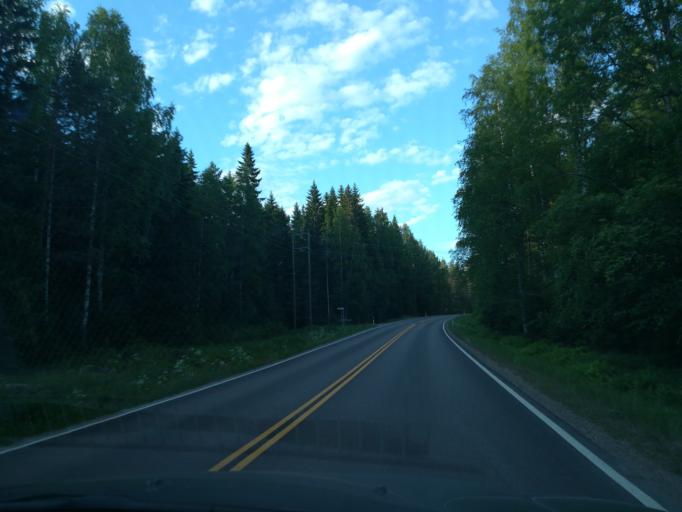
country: FI
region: Southern Savonia
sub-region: Mikkeli
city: Puumala
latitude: 61.5770
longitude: 28.1587
